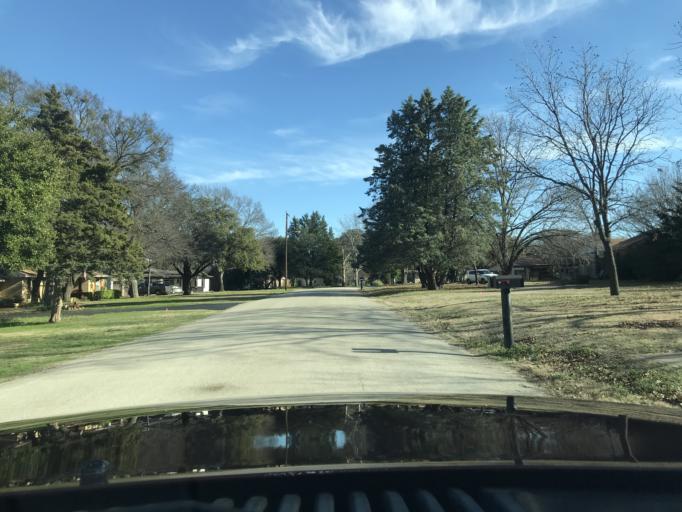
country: US
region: Texas
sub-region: Tarrant County
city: Edgecliff Village
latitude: 32.6607
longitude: -97.3422
